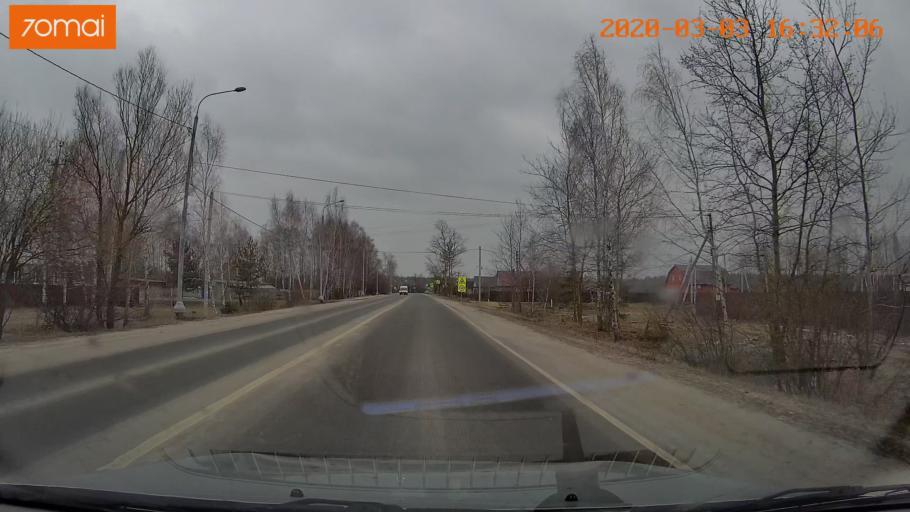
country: RU
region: Moskovskaya
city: Konobeyevo
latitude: 55.4223
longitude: 38.7307
